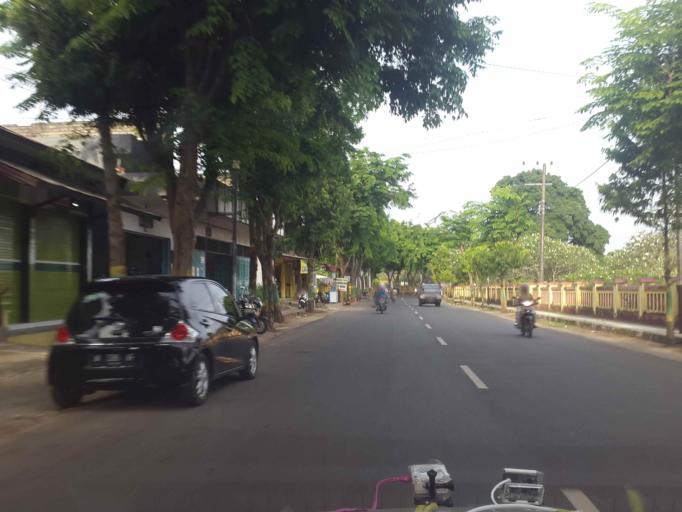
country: ID
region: East Java
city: Senmasen
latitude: -7.0008
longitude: 113.8621
